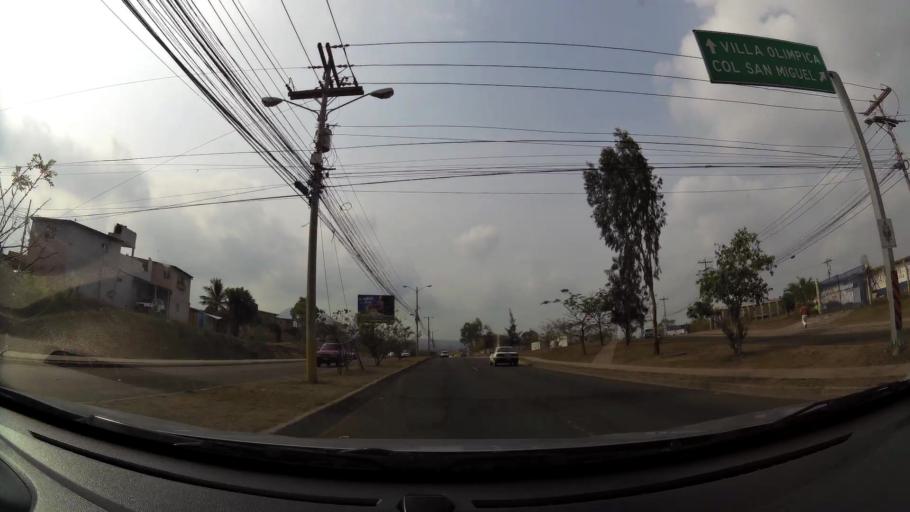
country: HN
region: Francisco Morazan
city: Santa Lucia
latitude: 14.1027
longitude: -87.1595
